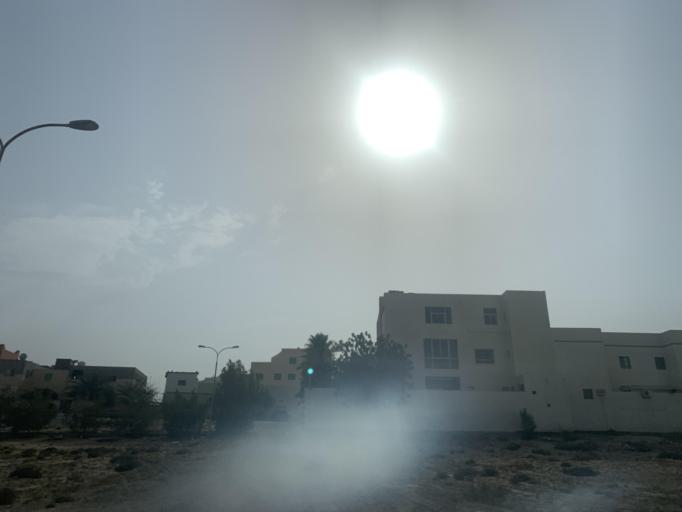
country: BH
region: Northern
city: Madinat `Isa
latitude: 26.1875
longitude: 50.4885
